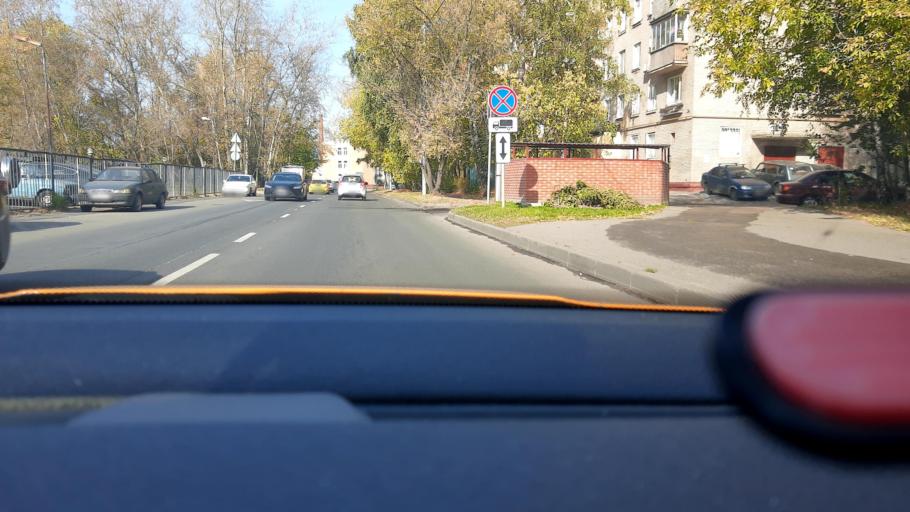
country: RU
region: Moscow
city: Vagonoremont
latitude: 55.8961
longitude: 37.5297
